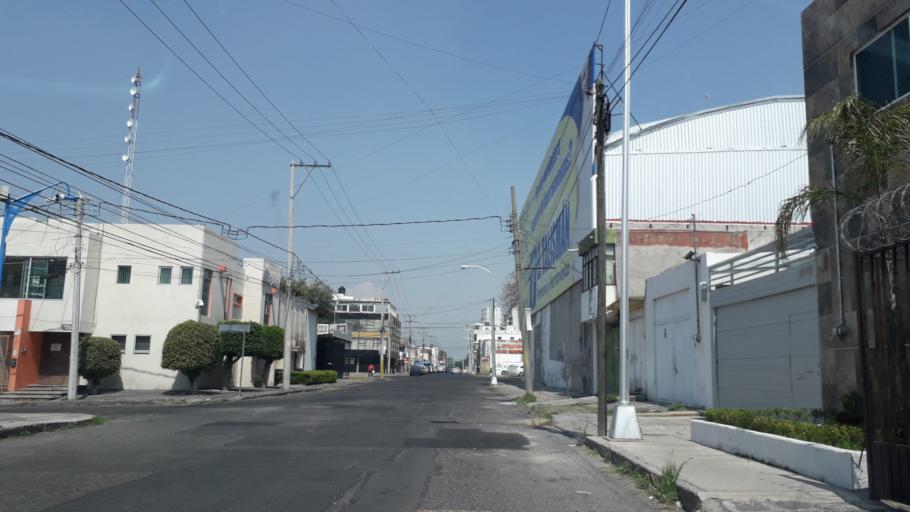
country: MX
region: Puebla
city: Puebla
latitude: 19.0546
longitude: -98.2186
